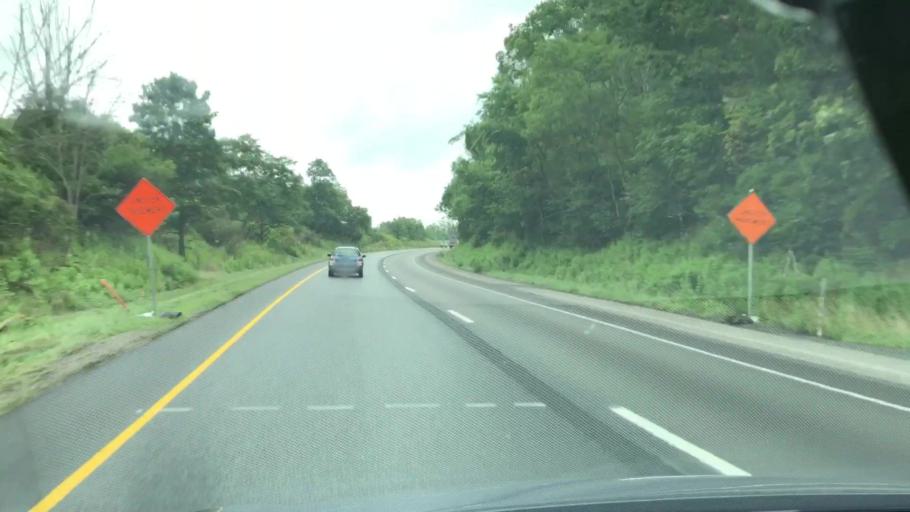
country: US
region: Pennsylvania
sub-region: Butler County
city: Slippery Rock
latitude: 40.9842
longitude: -80.1330
